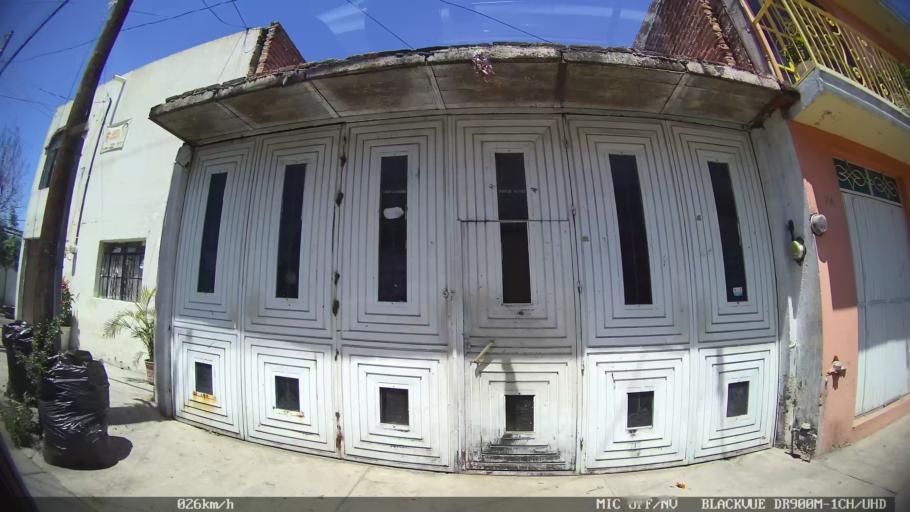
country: MX
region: Jalisco
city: Tlaquepaque
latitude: 20.6604
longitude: -103.2741
